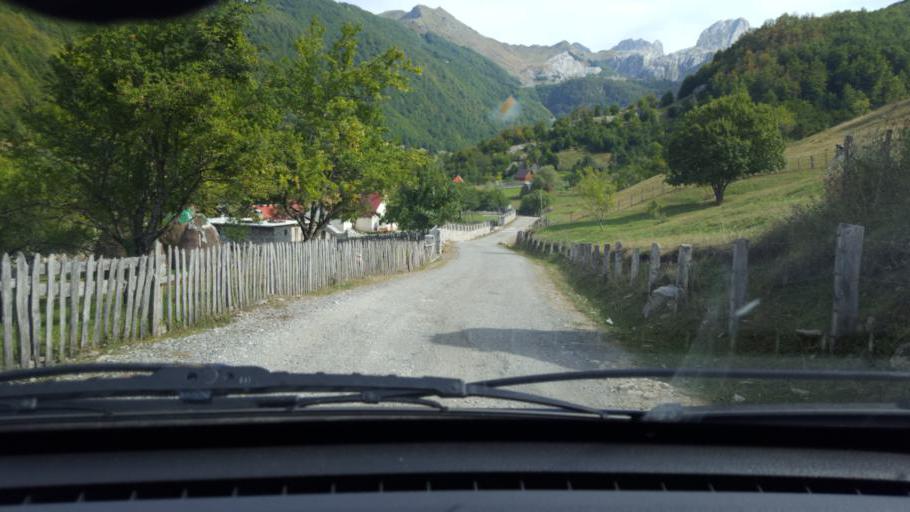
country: AL
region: Kukes
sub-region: Rrethi i Tropojes
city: Valbone
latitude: 42.5295
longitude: 19.7253
